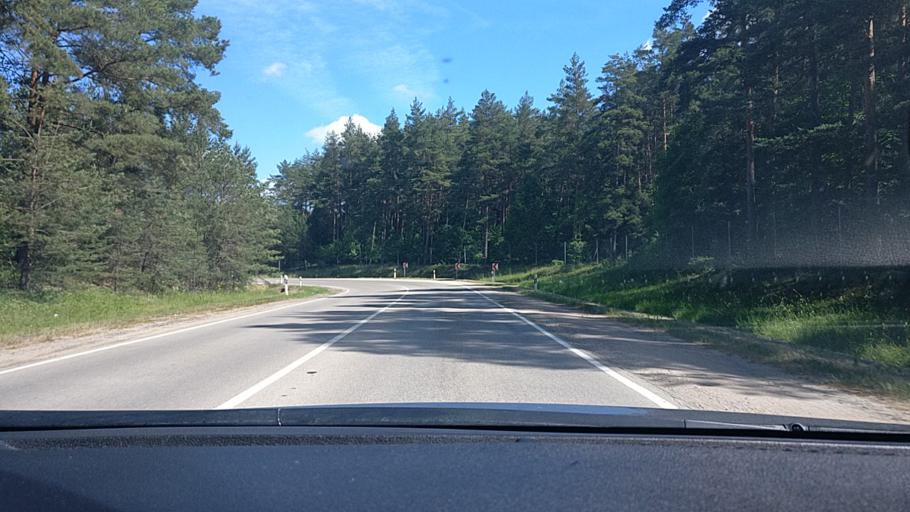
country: LT
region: Vilnius County
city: Ukmerge
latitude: 55.2708
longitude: 24.8130
